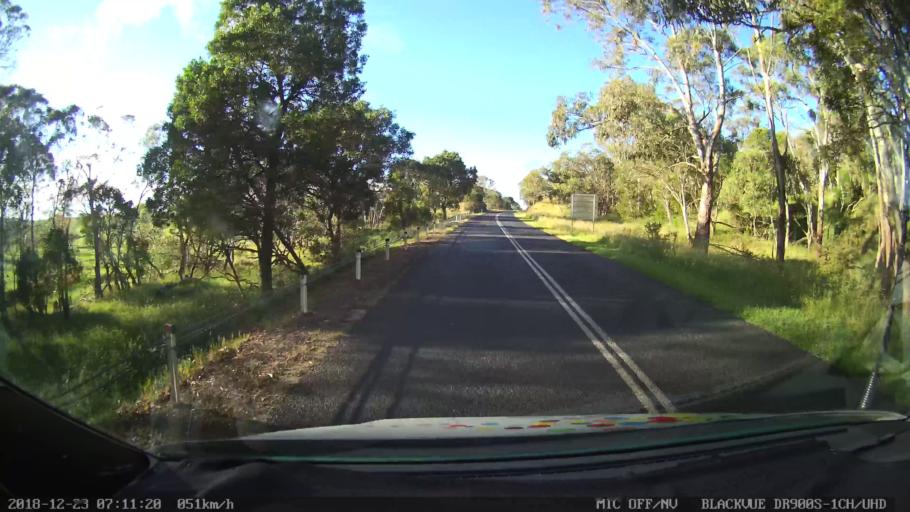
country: AU
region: New South Wales
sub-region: Bellingen
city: Dorrigo
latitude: -30.4012
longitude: 152.3475
